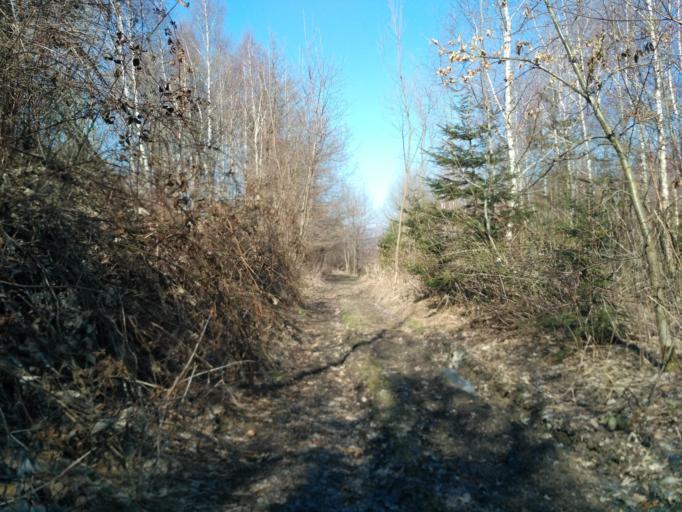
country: PL
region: Subcarpathian Voivodeship
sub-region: Powiat brzozowski
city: Golcowa
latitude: 49.7573
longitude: 22.0338
